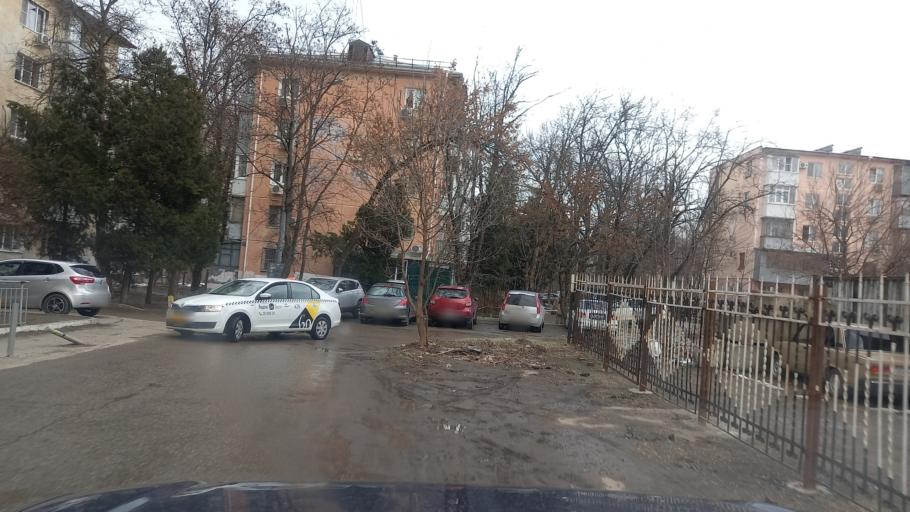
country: RU
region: Krasnodarskiy
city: Krasnodar
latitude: 45.0186
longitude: 39.0374
